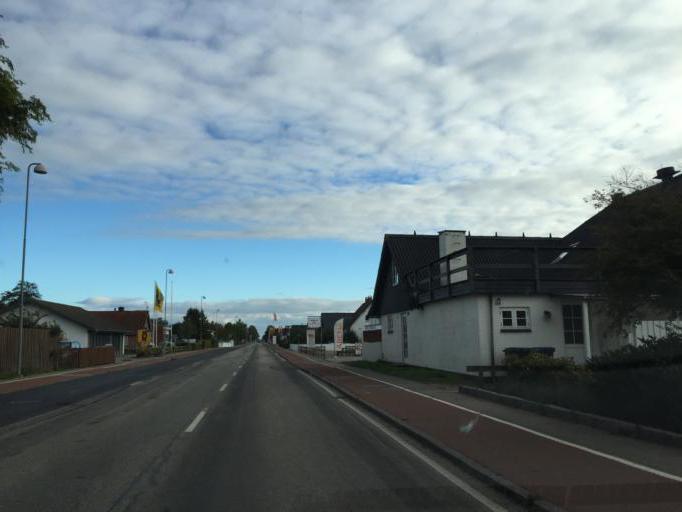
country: DK
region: Zealand
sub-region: Odsherred Kommune
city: Horve
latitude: 55.7882
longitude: 11.4641
